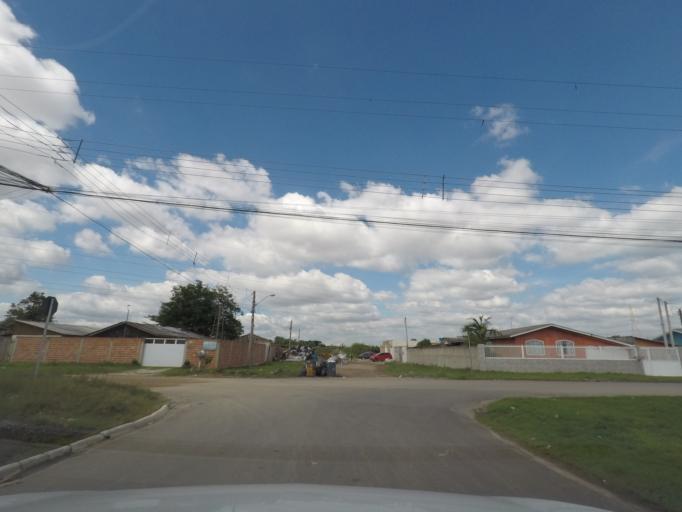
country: BR
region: Parana
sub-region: Sao Jose Dos Pinhais
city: Sao Jose dos Pinhais
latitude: -25.5105
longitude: -49.2175
